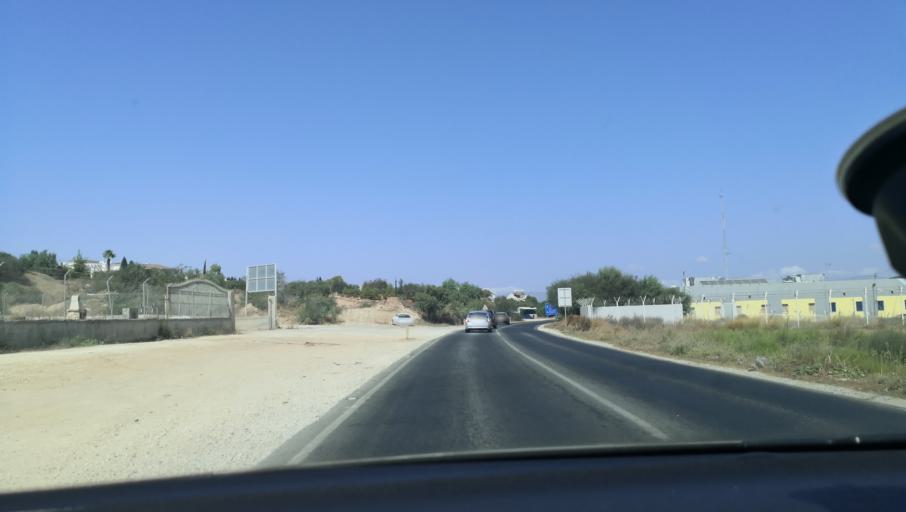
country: CY
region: Lefkosia
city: Kato Deftera
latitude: 35.1098
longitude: 33.2846
